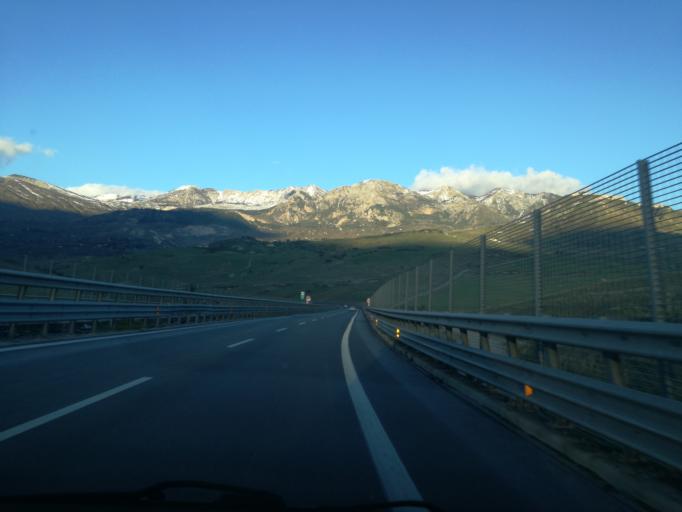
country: IT
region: Sicily
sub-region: Palermo
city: Polizzi Generosa
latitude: 37.8054
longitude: 13.9690
